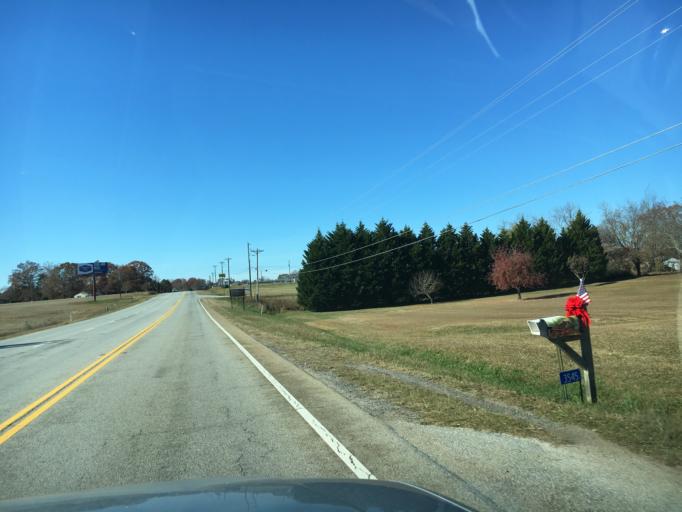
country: US
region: Georgia
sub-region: Hart County
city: Hartwell
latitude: 34.3459
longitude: -82.8705
